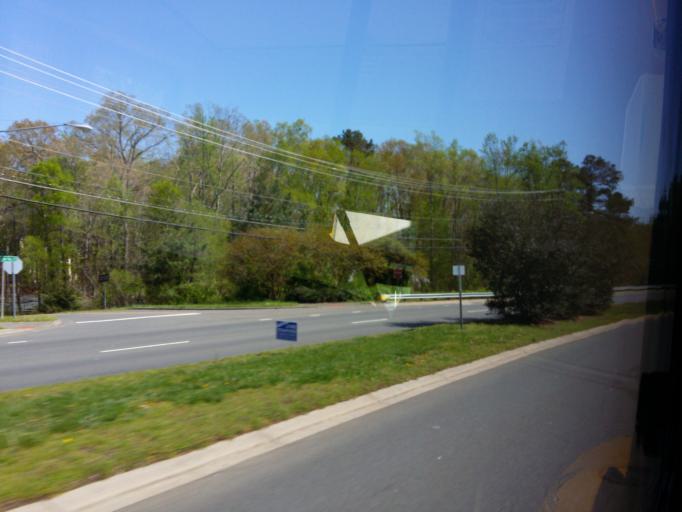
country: US
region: North Carolina
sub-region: Orange County
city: Chapel Hill
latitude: 35.9530
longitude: -79.0578
